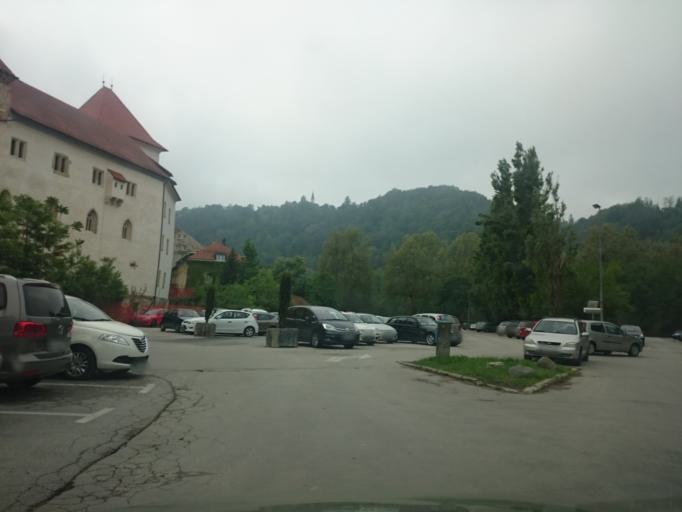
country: SI
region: Celje
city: Celje
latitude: 46.2294
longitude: 15.2601
